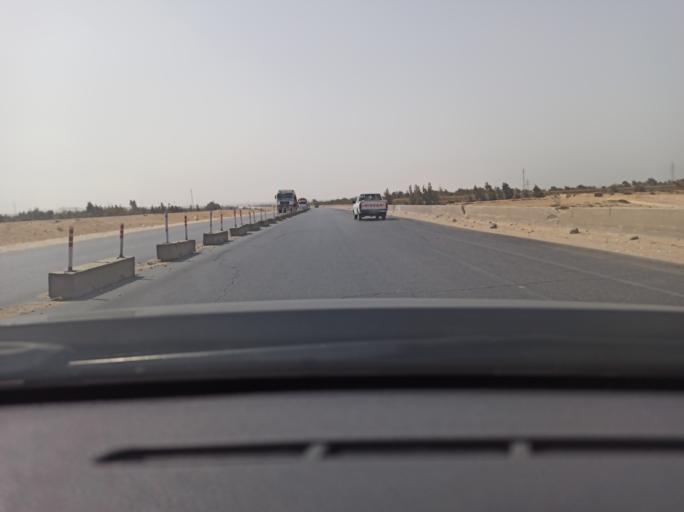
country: EG
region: Muhafazat al Fayyum
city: Al Wasitah
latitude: 29.2773
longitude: 31.2665
